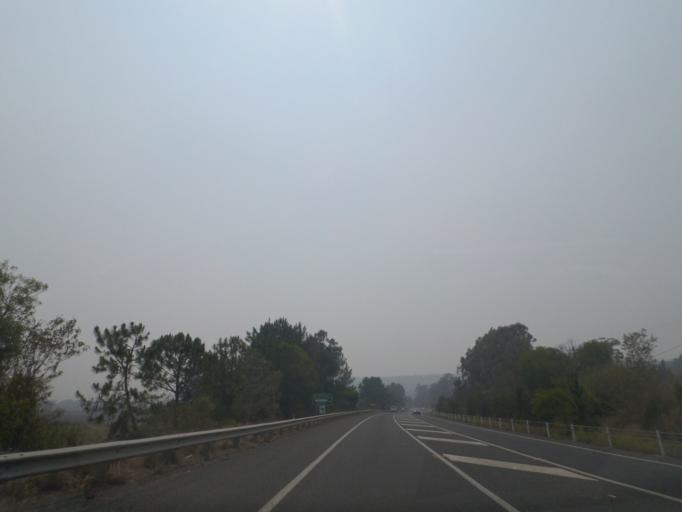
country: AU
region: New South Wales
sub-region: Clarence Valley
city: Maclean
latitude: -29.5648
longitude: 153.1408
